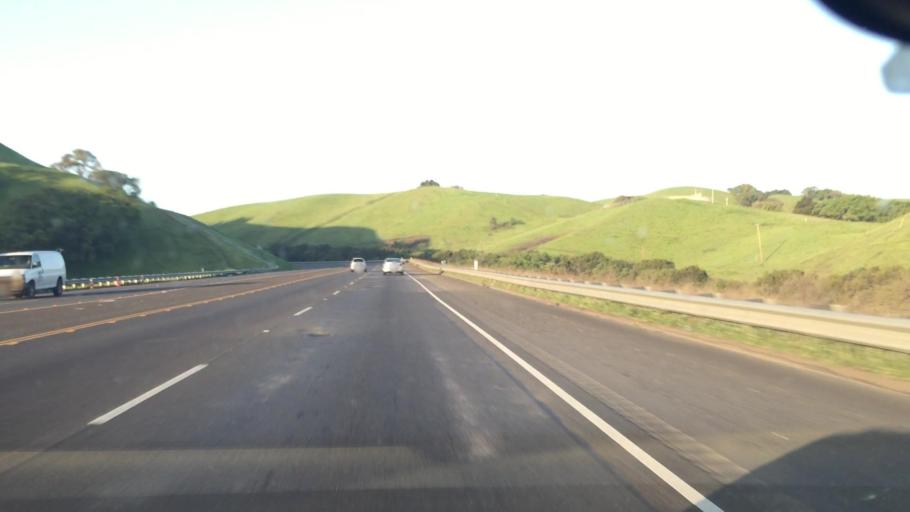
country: US
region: California
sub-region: Alameda County
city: Livermore
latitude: 37.6265
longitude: -121.8050
